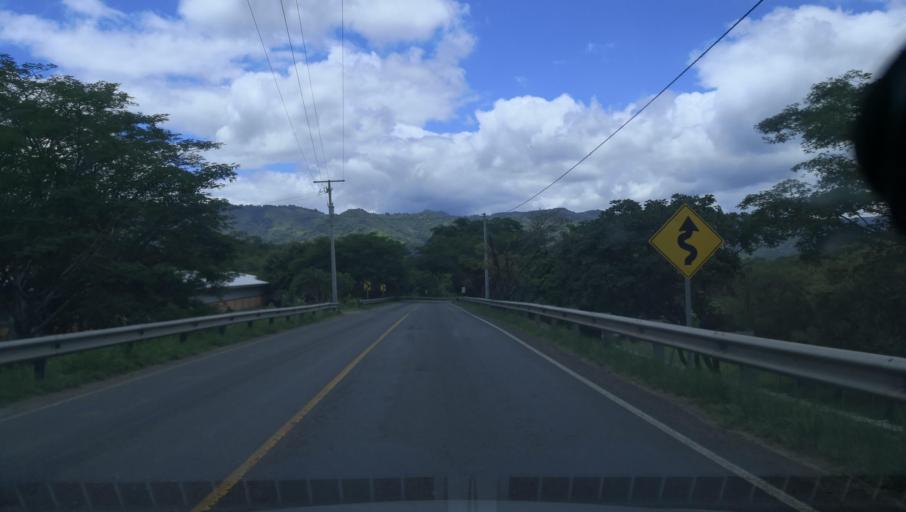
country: NI
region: Esteli
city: Condega
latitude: 13.2499
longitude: -86.3640
